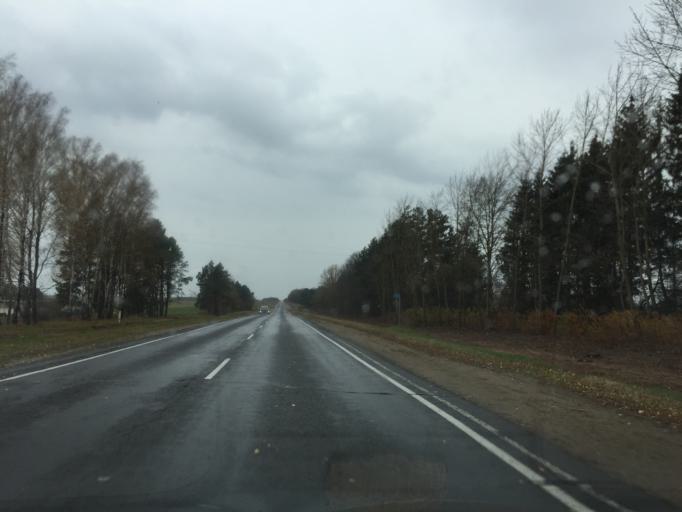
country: BY
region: Mogilev
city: Slawharad
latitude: 53.3976
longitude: 30.9160
